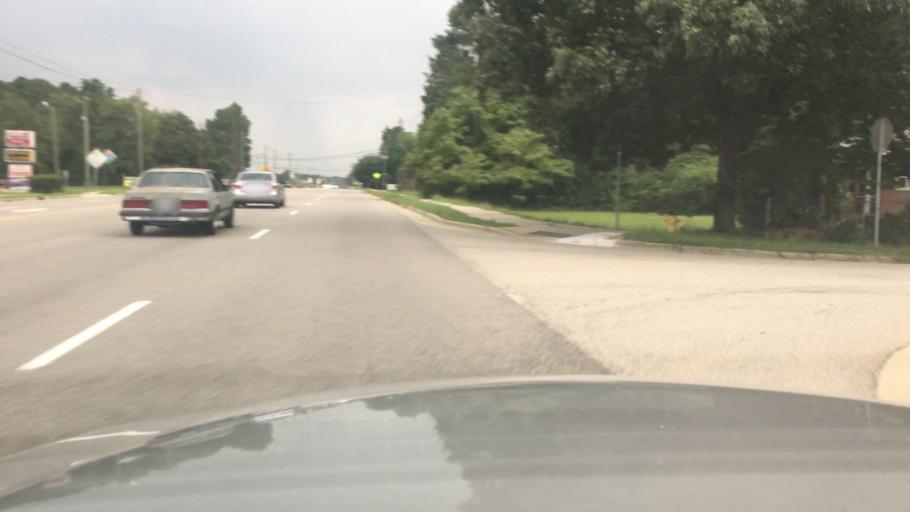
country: US
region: North Carolina
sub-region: Cumberland County
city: Fort Bragg
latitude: 35.0989
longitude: -79.0114
